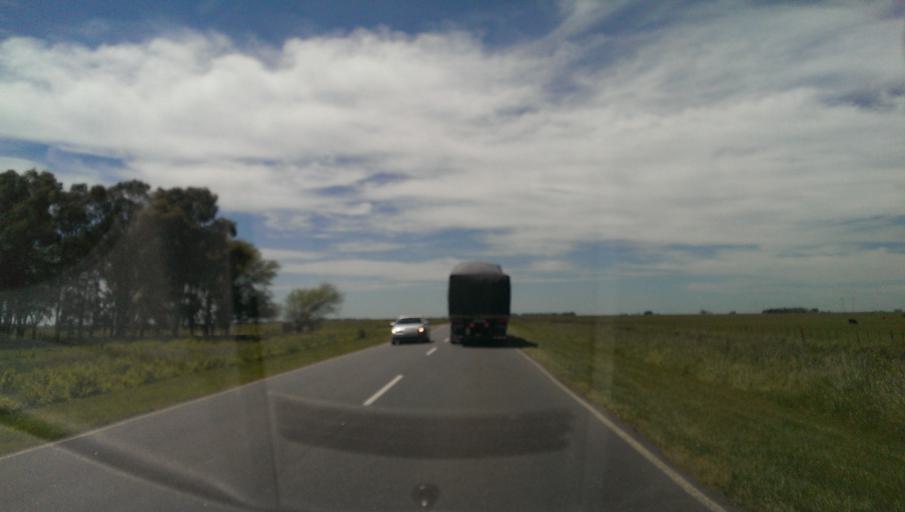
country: AR
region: Buenos Aires
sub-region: Partido de Laprida
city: Laprida
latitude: -37.2831
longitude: -60.8563
